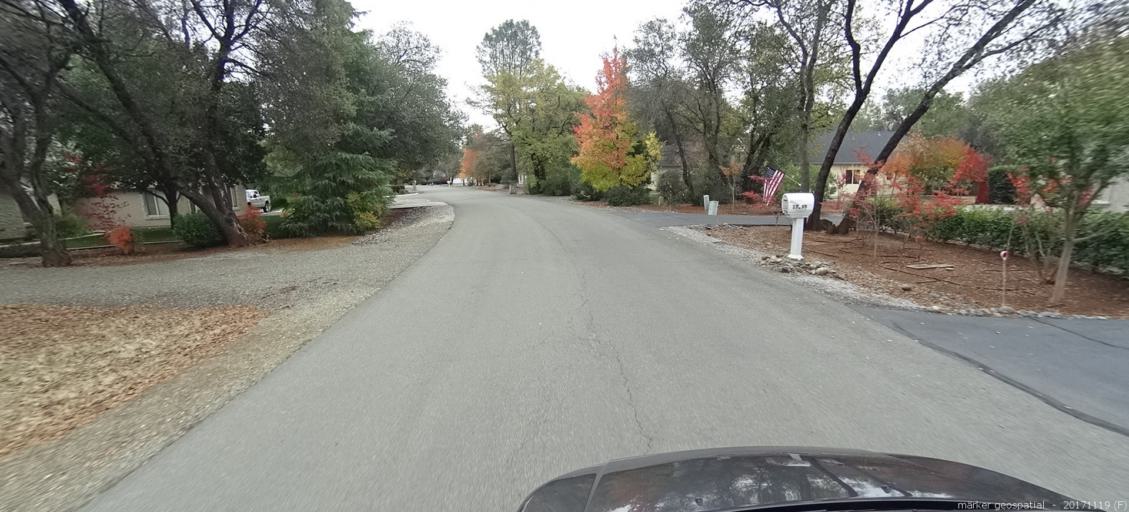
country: US
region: California
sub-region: Shasta County
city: Redding
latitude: 40.4940
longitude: -122.4087
